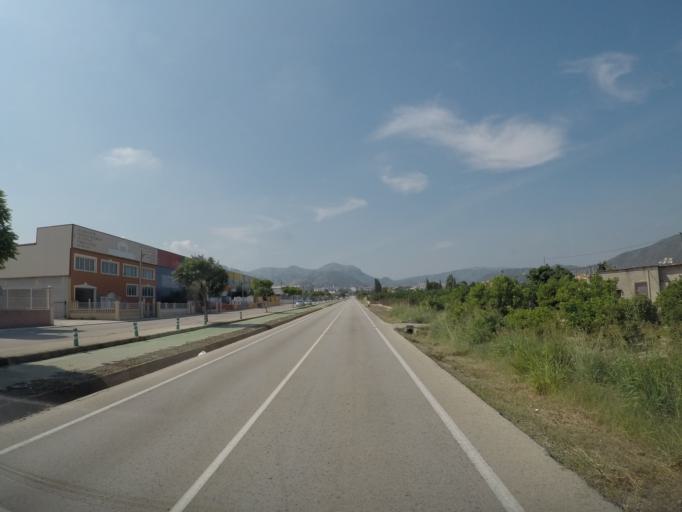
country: ES
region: Valencia
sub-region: Provincia de Alicante
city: Pego
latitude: 38.8453
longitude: -0.0982
